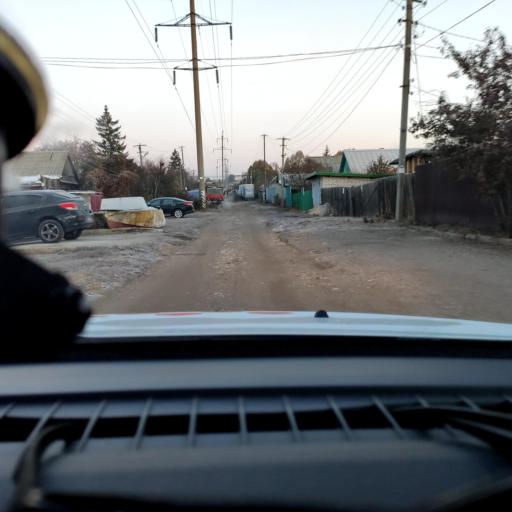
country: RU
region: Samara
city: Samara
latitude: 53.1749
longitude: 50.1826
